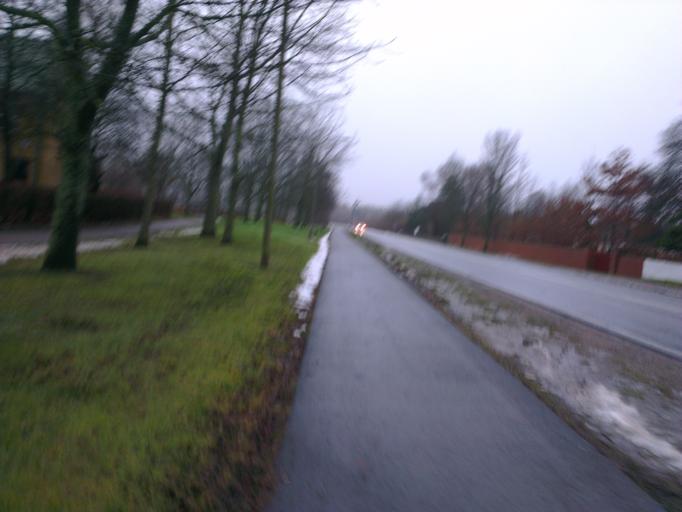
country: DK
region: Capital Region
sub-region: Frederikssund Kommune
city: Jaegerspris
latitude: 55.8411
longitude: 11.9881
